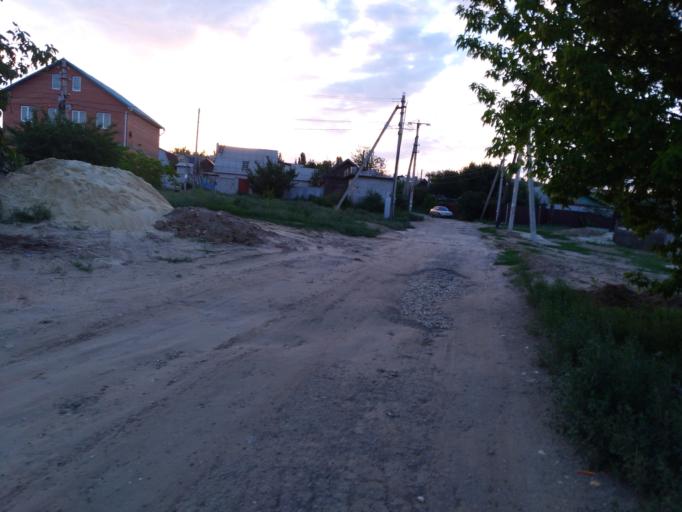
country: RU
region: Volgograd
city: Volgograd
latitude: 48.6694
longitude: 44.4528
